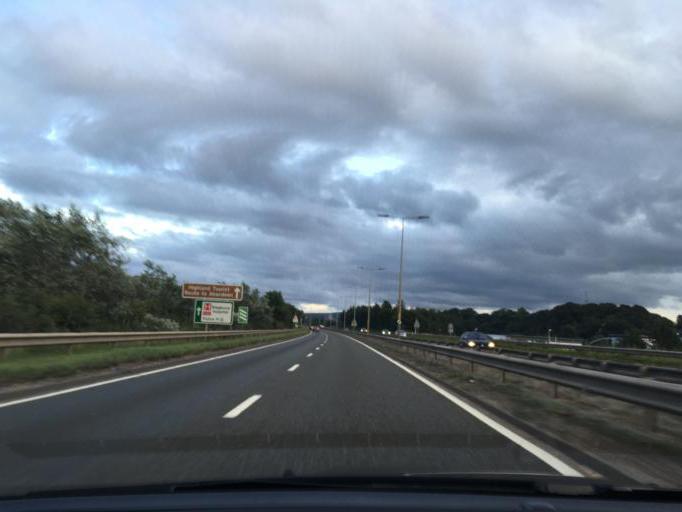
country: GB
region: Scotland
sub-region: Highland
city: Inverness
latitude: 57.4858
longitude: -4.2040
